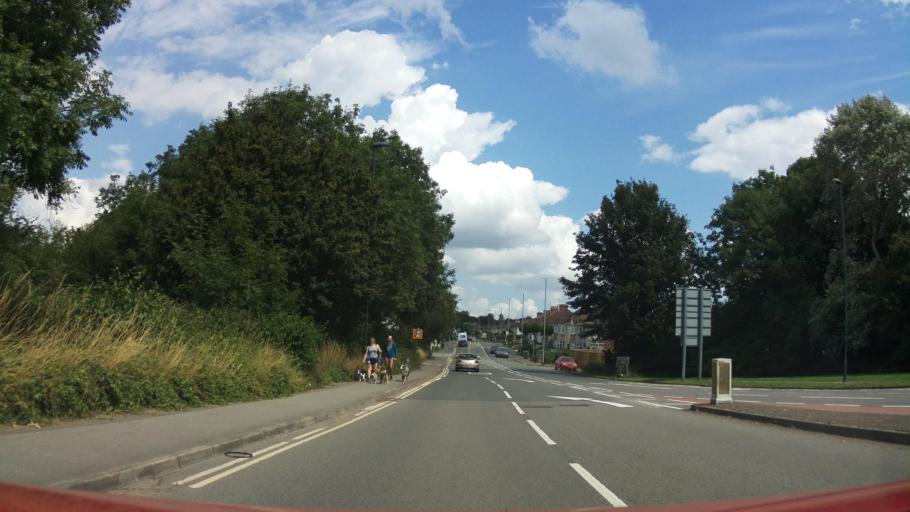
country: GB
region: England
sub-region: Borough of Swindon
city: Swindon
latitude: 51.5412
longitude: -1.7833
